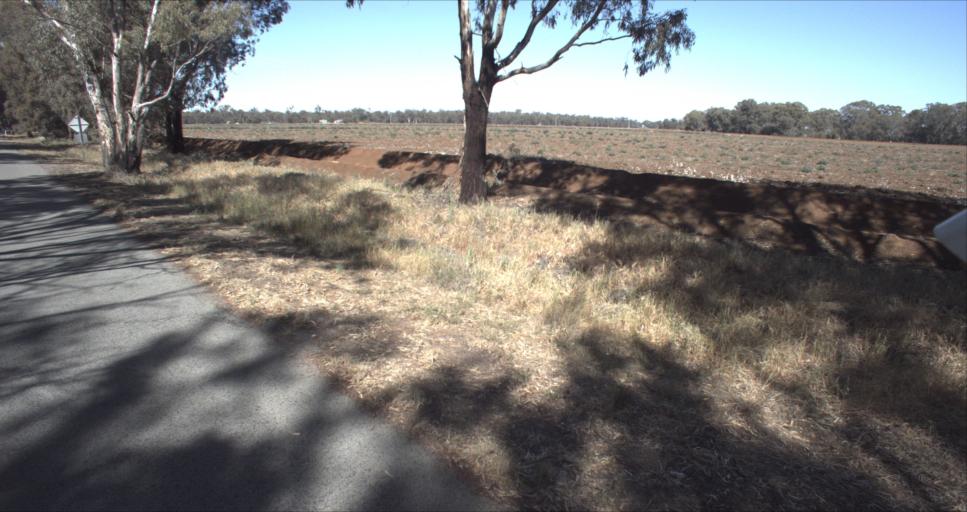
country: AU
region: New South Wales
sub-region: Leeton
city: Leeton
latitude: -34.6059
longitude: 146.2637
